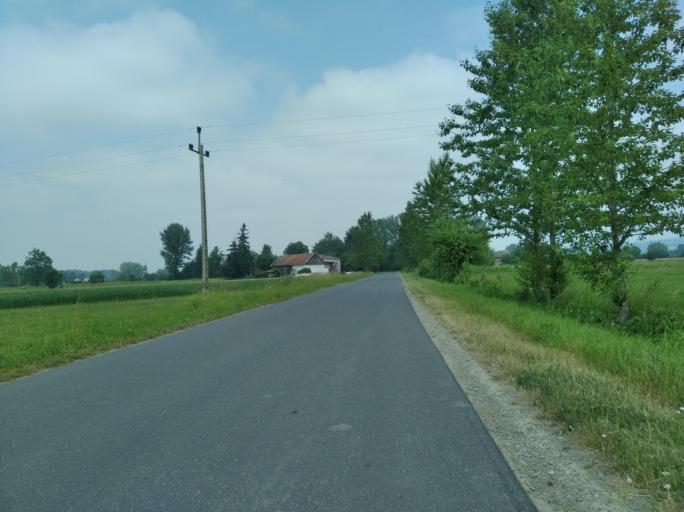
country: PL
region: Subcarpathian Voivodeship
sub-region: Powiat sanocki
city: Besko
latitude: 49.6213
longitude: 21.9369
